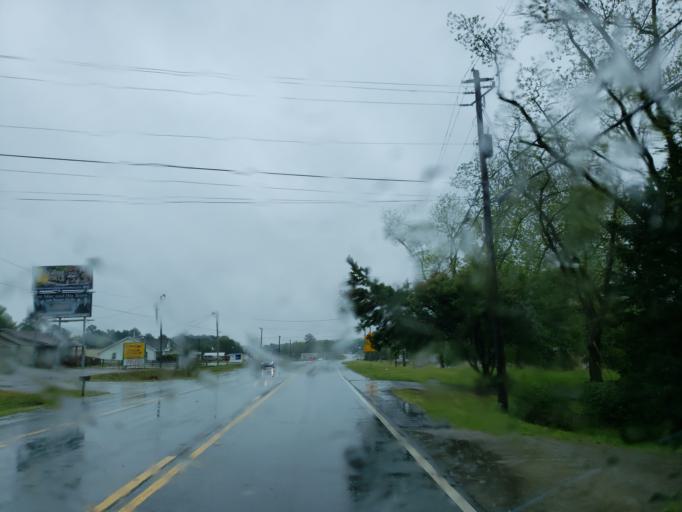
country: US
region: Georgia
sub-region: Carroll County
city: Villa Rica
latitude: 33.7317
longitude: -84.9483
